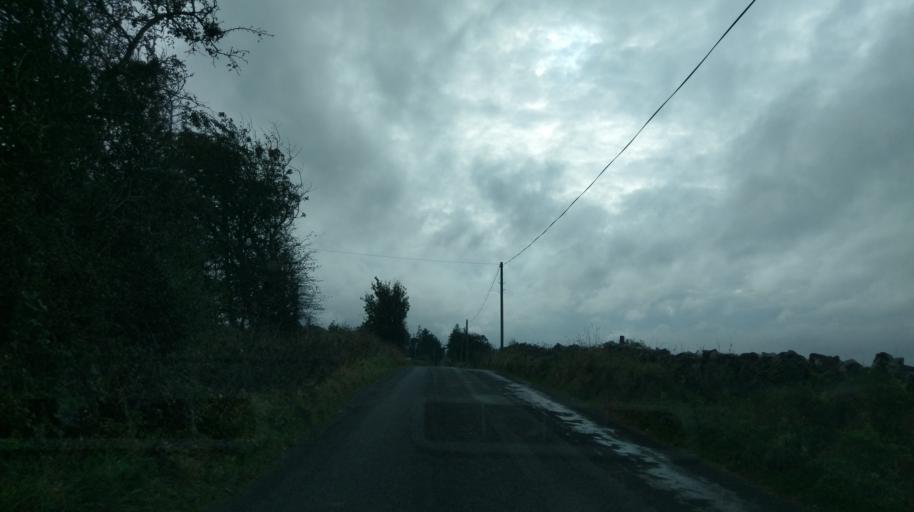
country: IE
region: Connaught
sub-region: County Galway
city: Athenry
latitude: 53.4487
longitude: -8.5708
